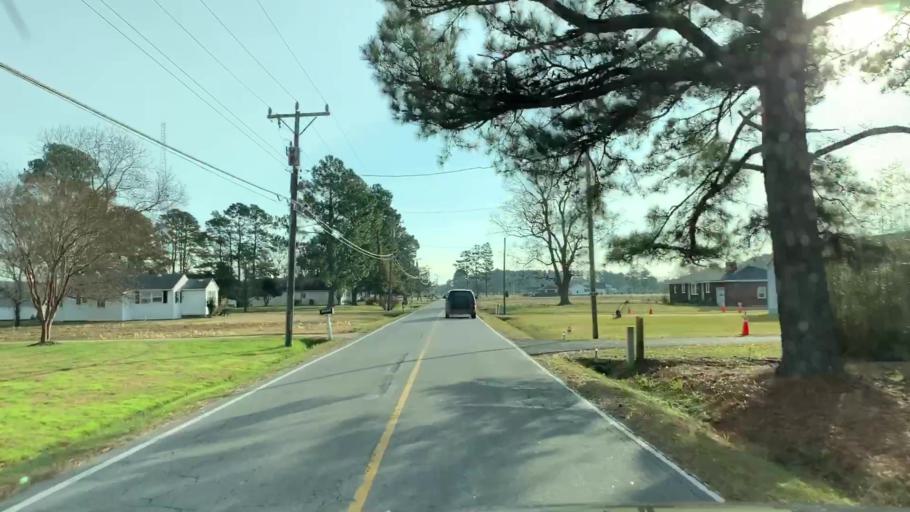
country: US
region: Virginia
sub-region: City of Virginia Beach
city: Virginia Beach
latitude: 36.6916
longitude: -76.0160
